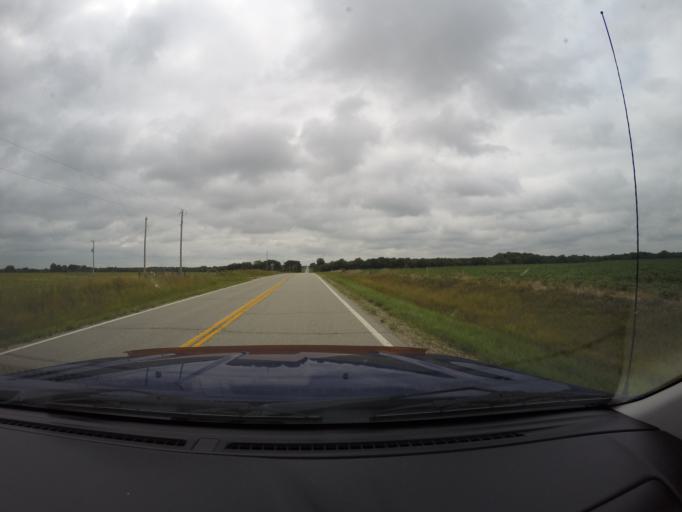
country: US
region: Kansas
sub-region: Morris County
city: Council Grove
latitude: 38.8410
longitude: -96.5582
